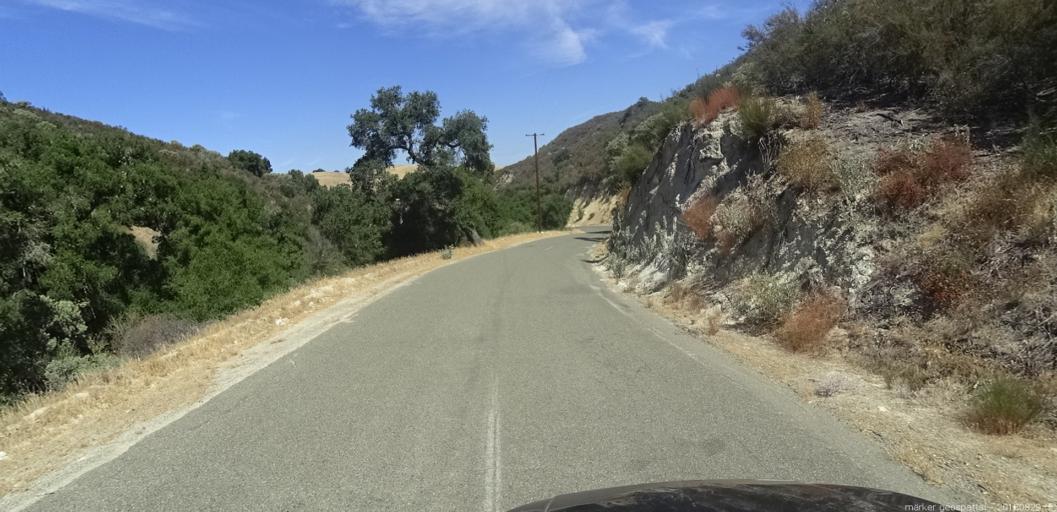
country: US
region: California
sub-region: San Luis Obispo County
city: Lake Nacimiento
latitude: 35.8277
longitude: -121.0495
